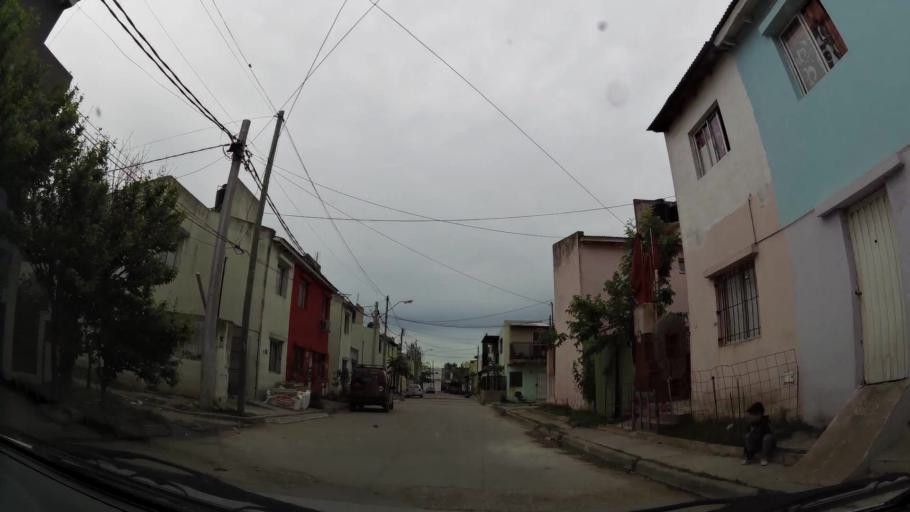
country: AR
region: Buenos Aires
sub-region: Partido de Avellaneda
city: Avellaneda
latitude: -34.6494
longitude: -58.3566
